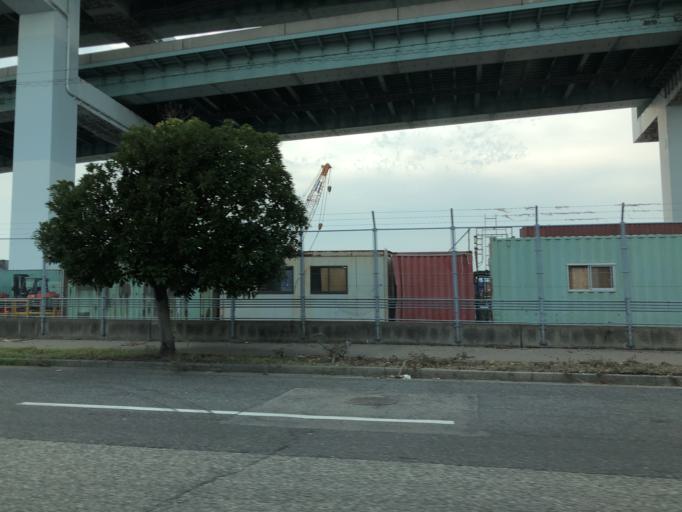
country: JP
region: Hyogo
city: Ashiya
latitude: 34.6975
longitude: 135.2737
